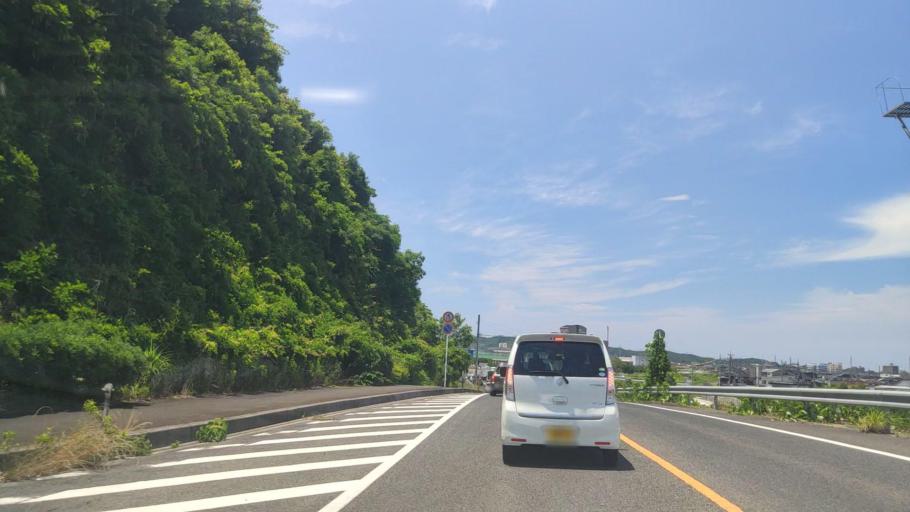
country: JP
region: Tottori
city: Tottori
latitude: 35.4722
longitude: 134.2404
